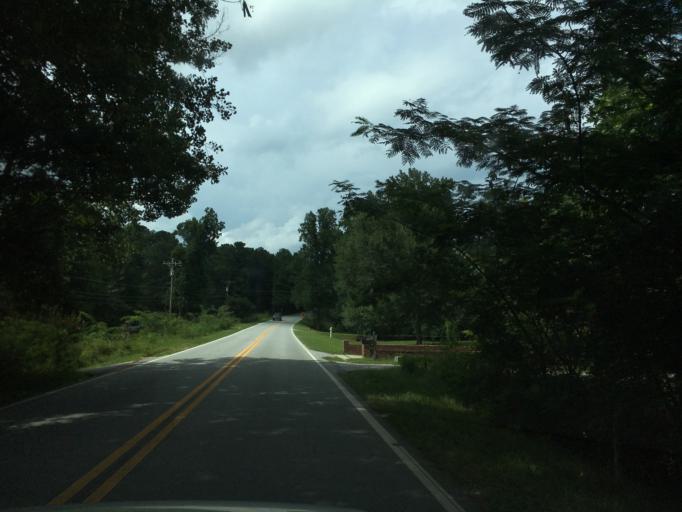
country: US
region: Georgia
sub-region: Rockdale County
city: Lakeview Estates
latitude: 33.7233
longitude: -84.0190
